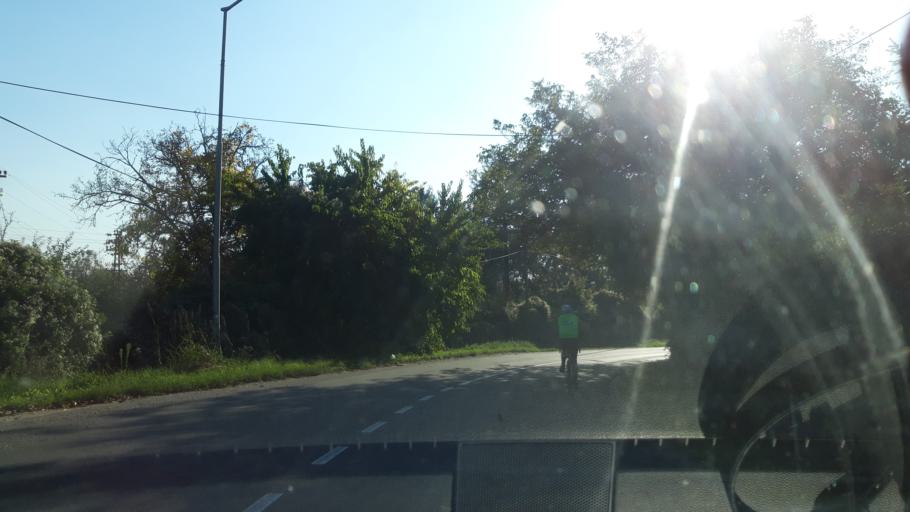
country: RS
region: Autonomna Pokrajina Vojvodina
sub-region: Juznobacki Okrug
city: Petrovaradin
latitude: 45.2381
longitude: 19.8661
